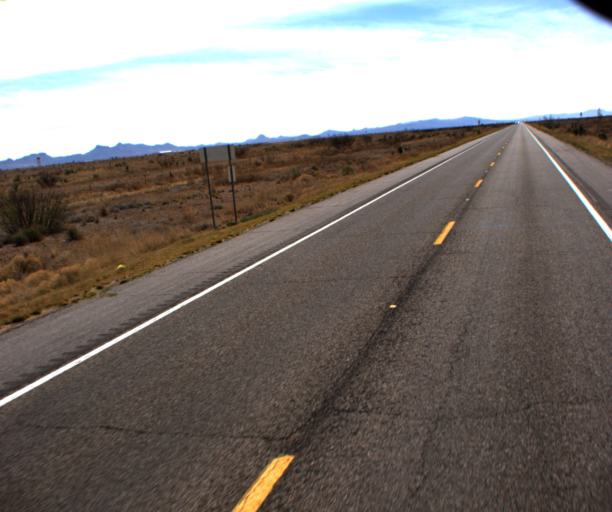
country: US
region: Arizona
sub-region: Cochise County
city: Pirtleville
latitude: 31.4722
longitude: -109.6199
